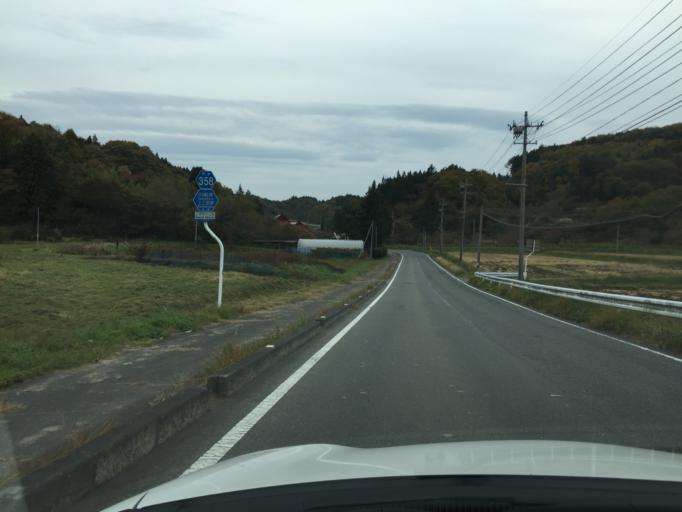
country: JP
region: Fukushima
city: Ishikawa
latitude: 37.1963
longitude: 140.6284
